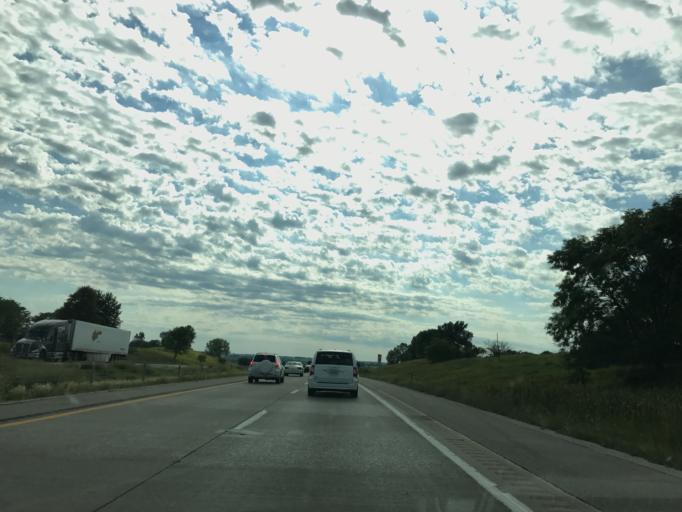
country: US
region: Iowa
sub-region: Dallas County
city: Van Meter
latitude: 41.5504
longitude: -93.9442
